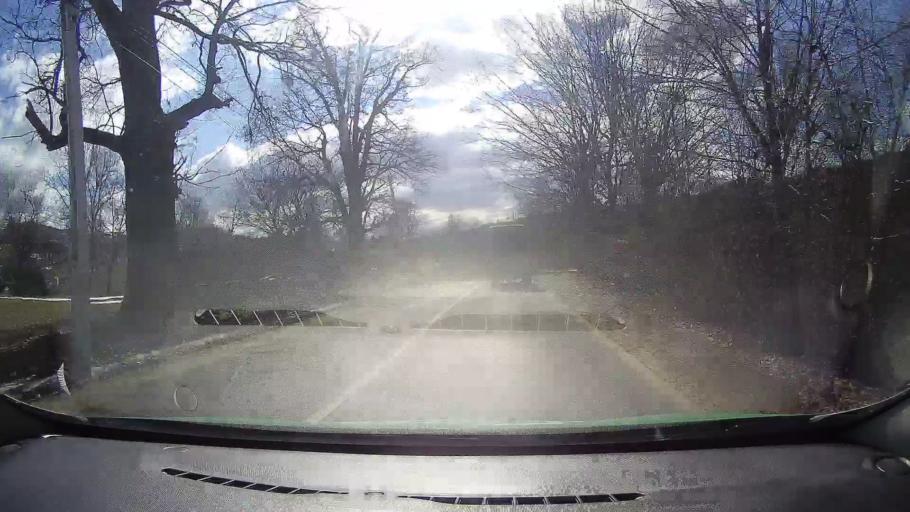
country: RO
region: Dambovita
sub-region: Comuna Runcu
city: Badeni
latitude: 45.1388
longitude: 25.4025
